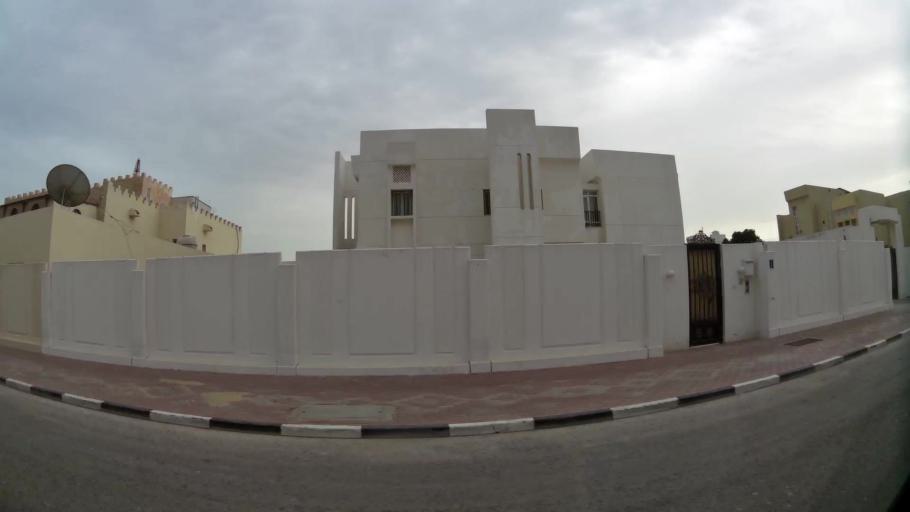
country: QA
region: Baladiyat ad Dawhah
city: Doha
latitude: 25.3318
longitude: 51.5085
